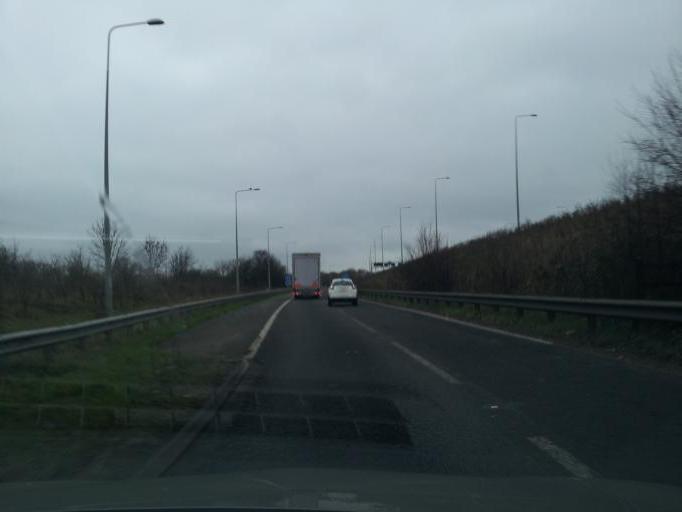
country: GB
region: England
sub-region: Nottinghamshire
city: Kimberley
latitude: 52.9891
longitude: -1.2343
